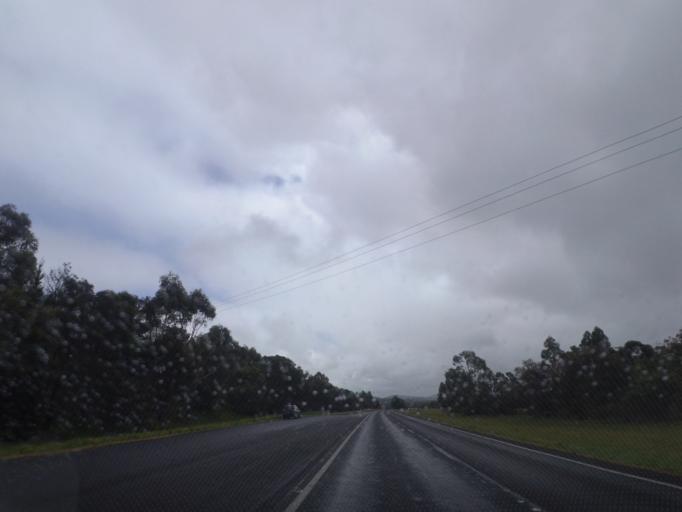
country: AU
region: Victoria
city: Black Hill
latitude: -37.5320
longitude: 143.8729
